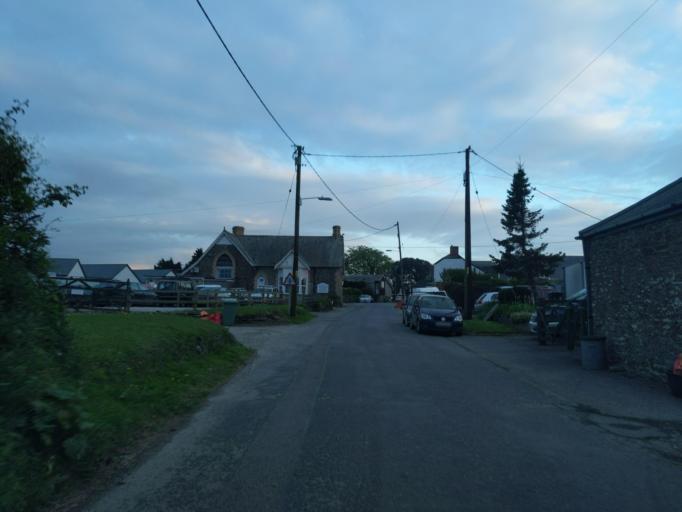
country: GB
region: England
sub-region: Cornwall
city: Polzeath
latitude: 50.5594
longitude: -4.8729
